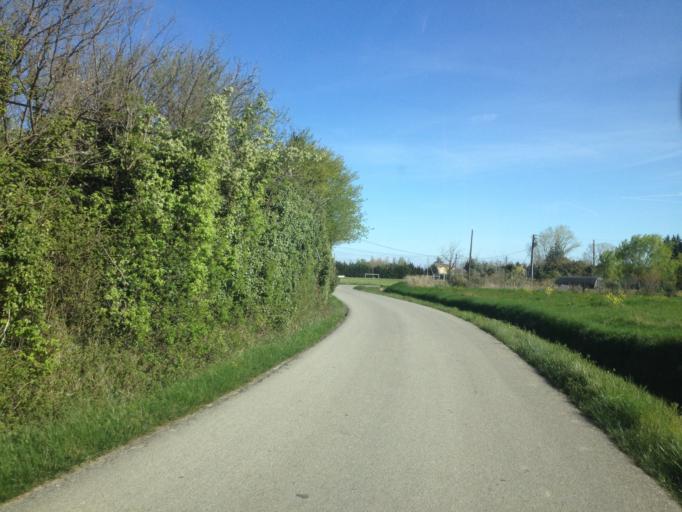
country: FR
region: Provence-Alpes-Cote d'Azur
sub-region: Departement du Vaucluse
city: Caderousse
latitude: 44.1080
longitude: 4.7550
